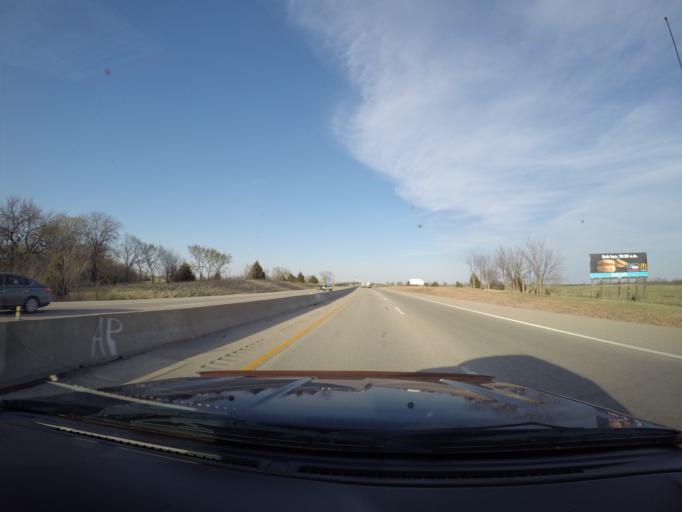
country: US
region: Kansas
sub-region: Douglas County
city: Eudora
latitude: 39.0123
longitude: -95.1485
